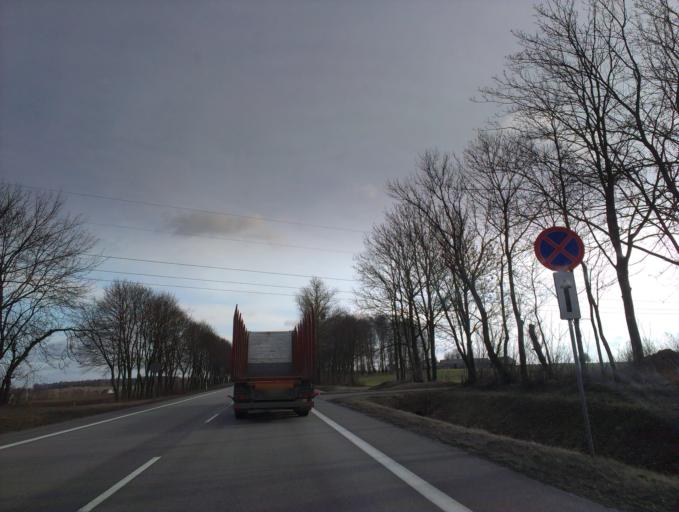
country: PL
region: Kujawsko-Pomorskie
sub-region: Powiat lipnowski
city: Kikol
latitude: 52.8800
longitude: 19.1414
